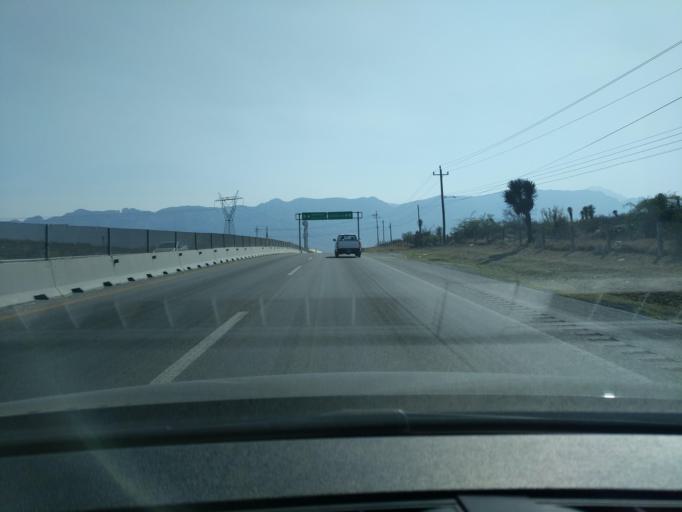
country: MX
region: Nuevo Leon
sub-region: Garcia
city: Los Parques
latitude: 25.7464
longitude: -100.5118
